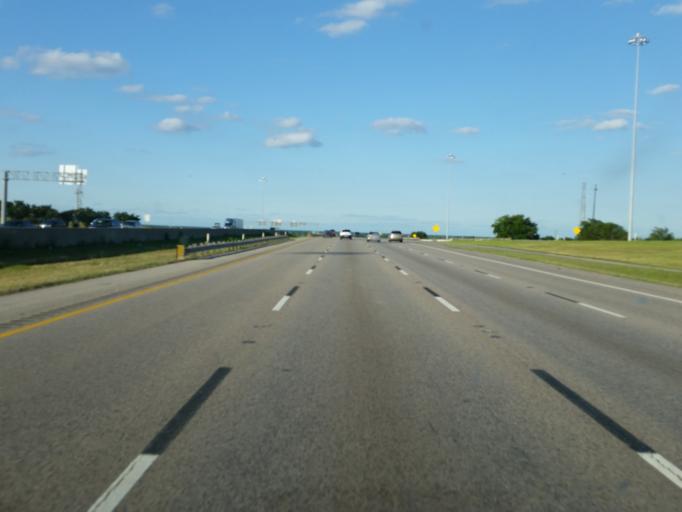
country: US
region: Texas
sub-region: Dallas County
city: Hutchins
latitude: 32.6624
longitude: -96.7252
